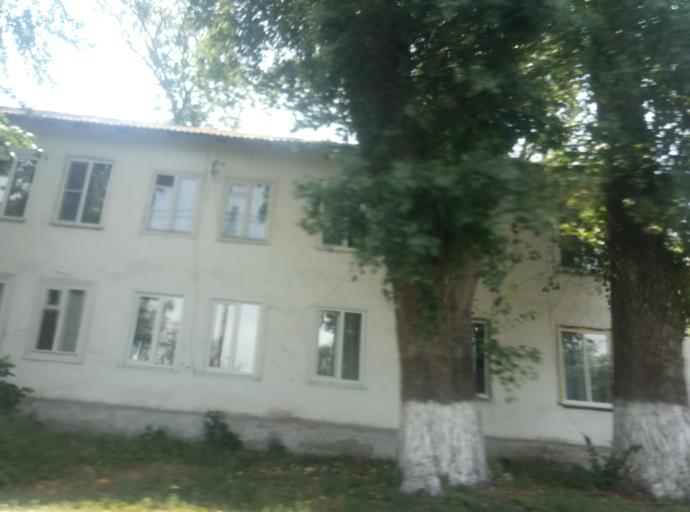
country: RU
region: Tula
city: Kireyevsk
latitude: 53.9316
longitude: 37.9354
